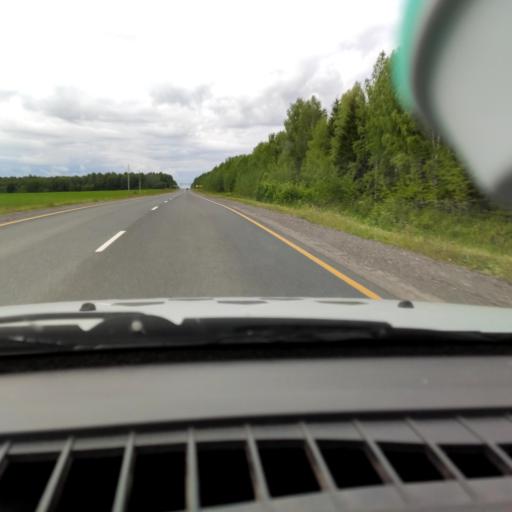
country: RU
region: Perm
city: Lys'va
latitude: 58.1721
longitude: 57.7827
